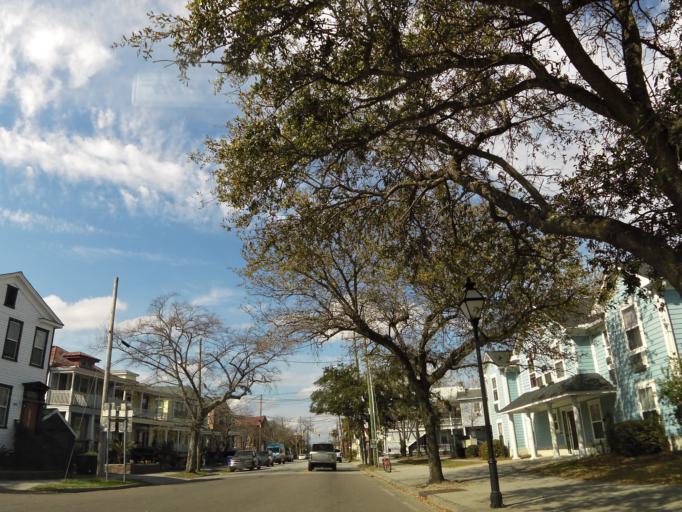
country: US
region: South Carolina
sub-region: Charleston County
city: Charleston
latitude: 32.7970
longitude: -79.9448
